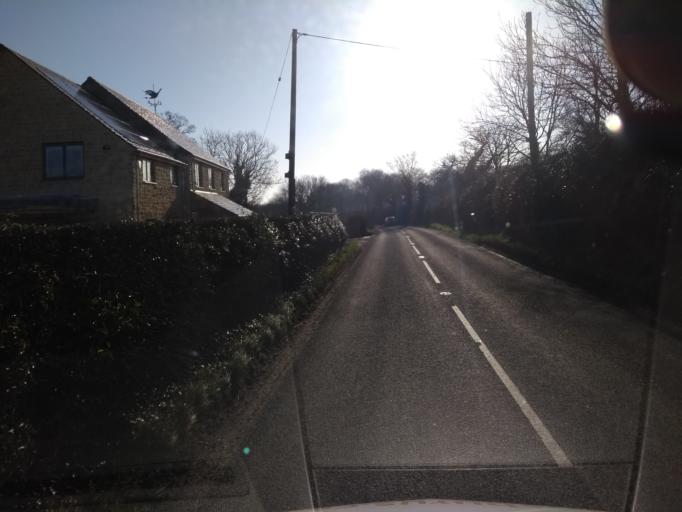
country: GB
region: England
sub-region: Somerset
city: Redlynch
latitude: 51.1005
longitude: -2.4292
